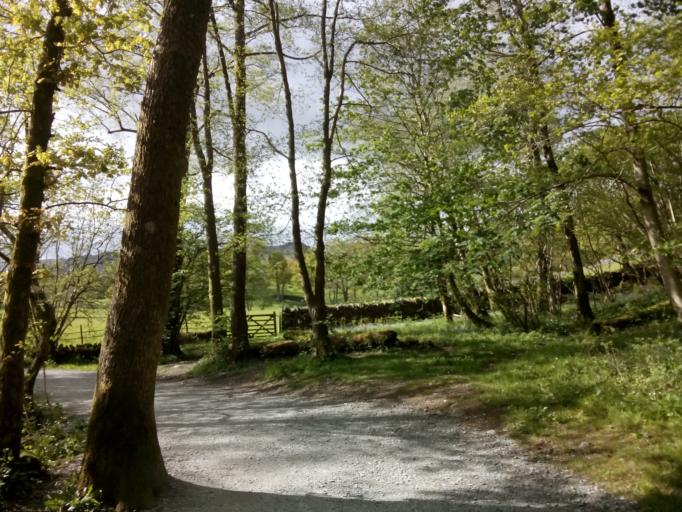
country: GB
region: England
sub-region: Cumbria
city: Ambleside
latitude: 54.4292
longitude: -3.0230
